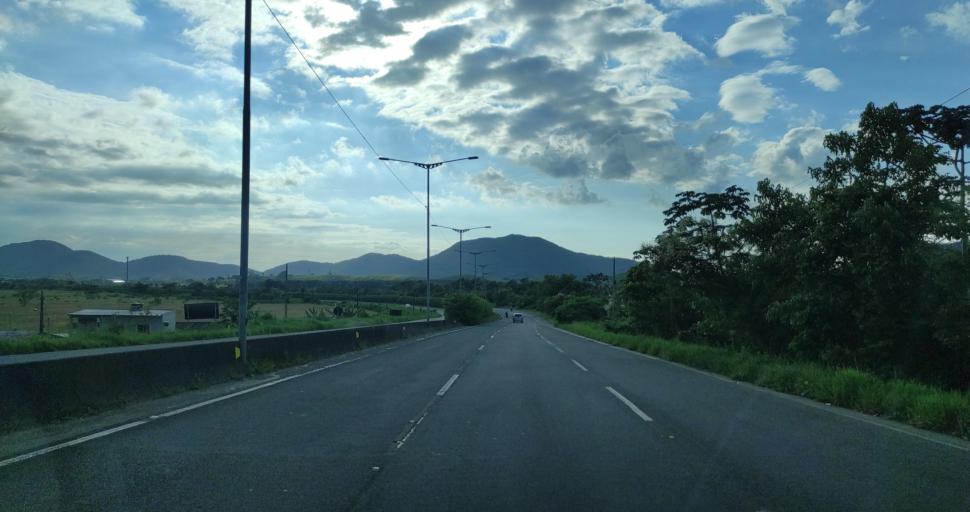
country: BR
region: Santa Catarina
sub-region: Penha
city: Penha
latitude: -26.8054
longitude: -48.6433
